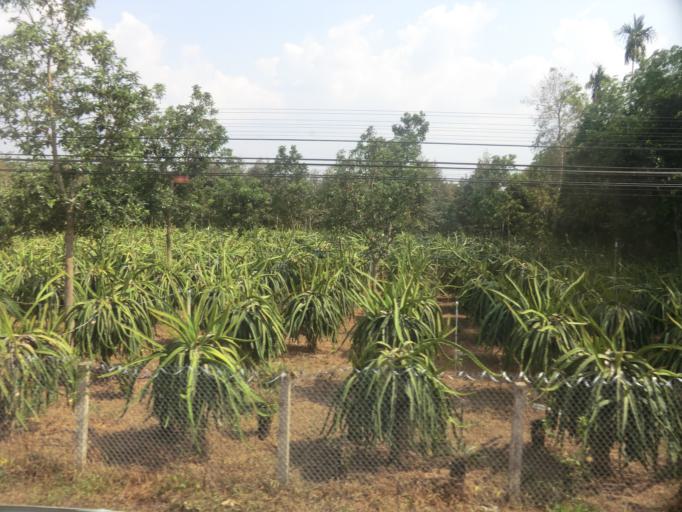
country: VN
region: Dong Nai
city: Long Khanh
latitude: 10.9286
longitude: 107.2001
